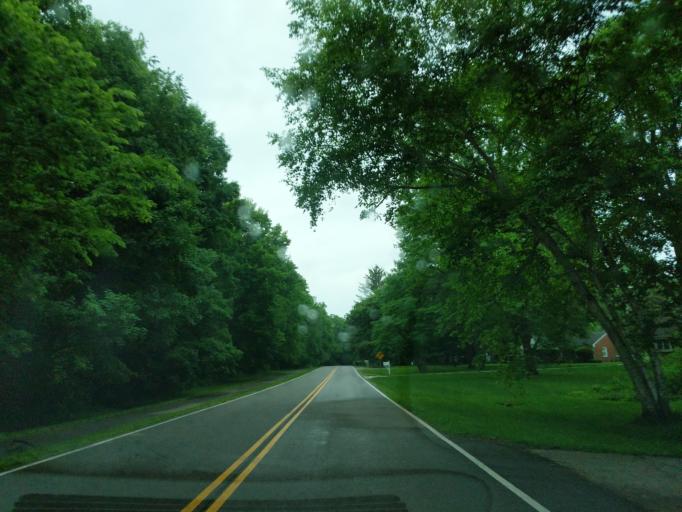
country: US
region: Indiana
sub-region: Madison County
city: Chesterfield
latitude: 40.0968
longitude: -85.6176
